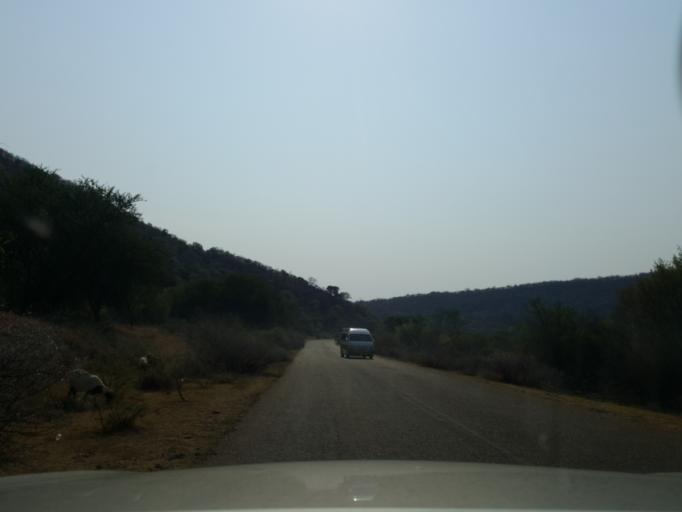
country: BW
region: South East
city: Lobatse
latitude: -25.3289
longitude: 25.7847
